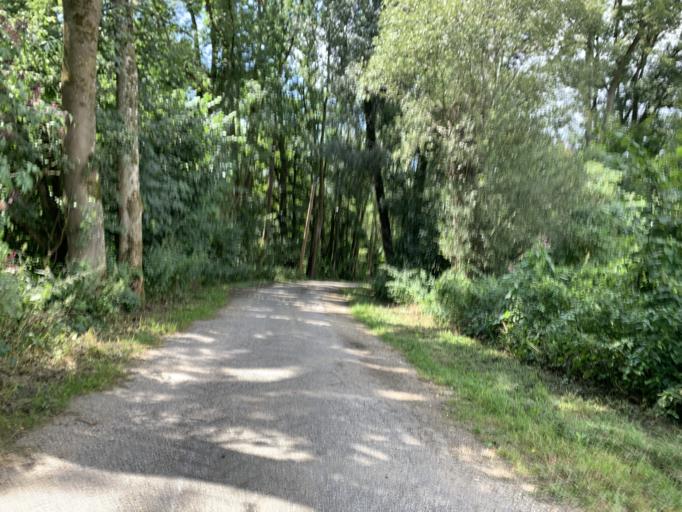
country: DE
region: Bavaria
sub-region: Upper Bavaria
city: Zolling
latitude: 48.4495
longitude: 11.7575
